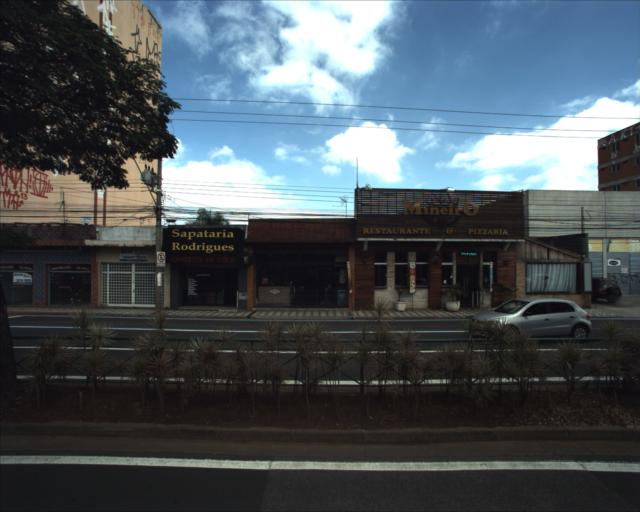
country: BR
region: Sao Paulo
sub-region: Sorocaba
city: Sorocaba
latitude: -23.5043
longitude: -47.4764
